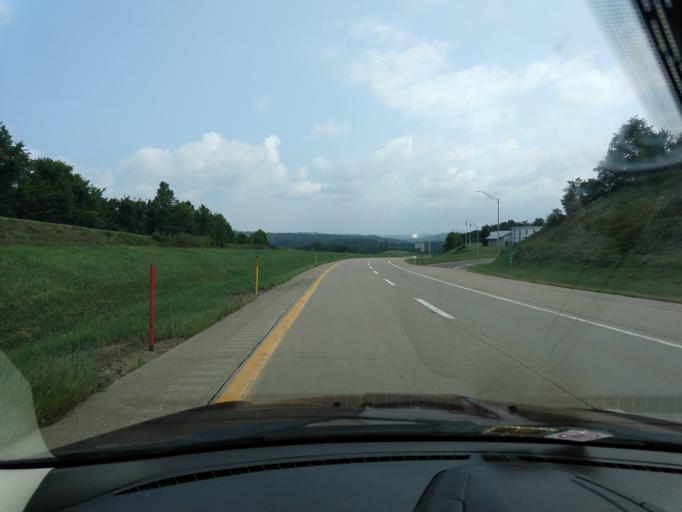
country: US
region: Pennsylvania
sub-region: Allegheny County
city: Jefferson Hills
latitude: 40.2752
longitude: -79.9552
